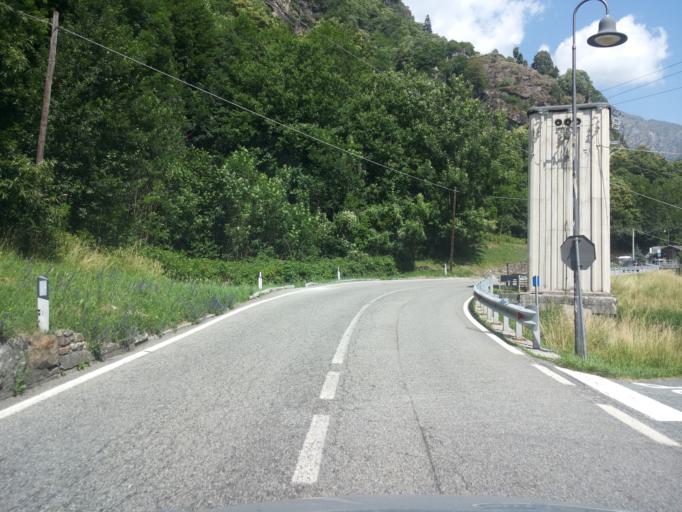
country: IT
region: Aosta Valley
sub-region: Valle d'Aosta
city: Fontainemore
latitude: 45.6619
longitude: 7.8580
